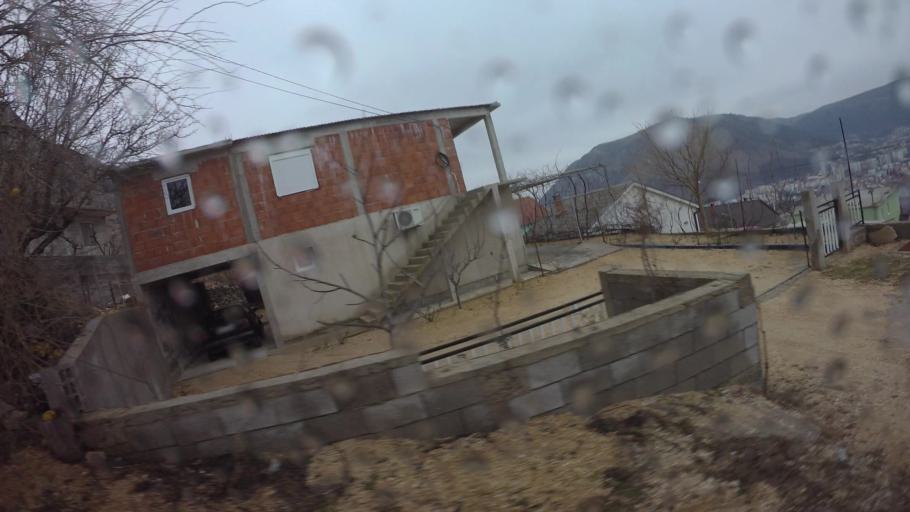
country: BA
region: Federation of Bosnia and Herzegovina
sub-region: Hercegovacko-Bosanski Kanton
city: Mostar
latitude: 43.3455
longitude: 17.8203
